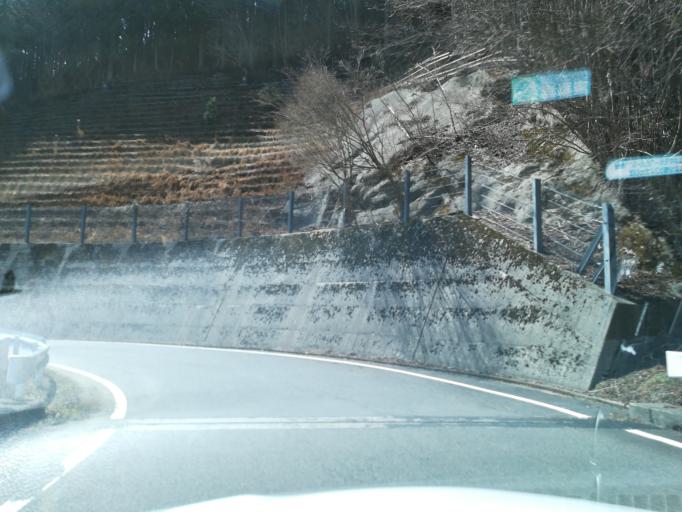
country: JP
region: Tokushima
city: Wakimachi
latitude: 33.8537
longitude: 134.0424
